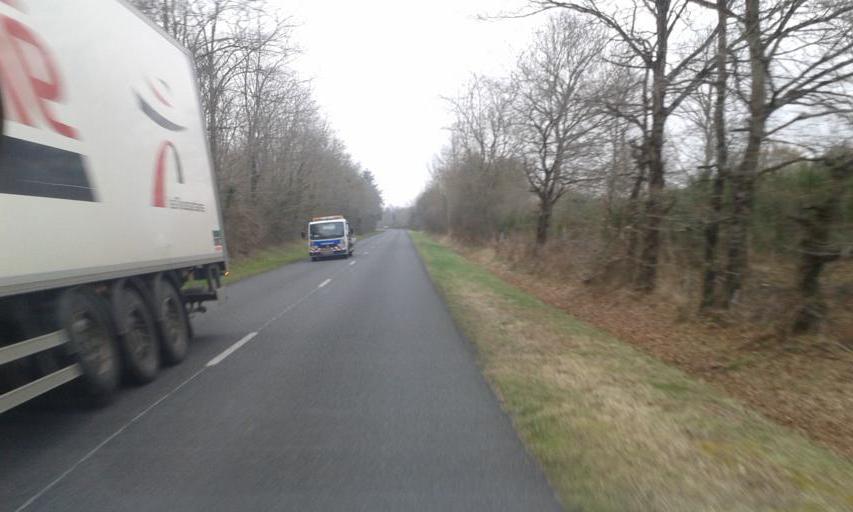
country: FR
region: Centre
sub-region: Departement du Loiret
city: Lailly-en-Val
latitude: 47.7250
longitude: 1.6559
